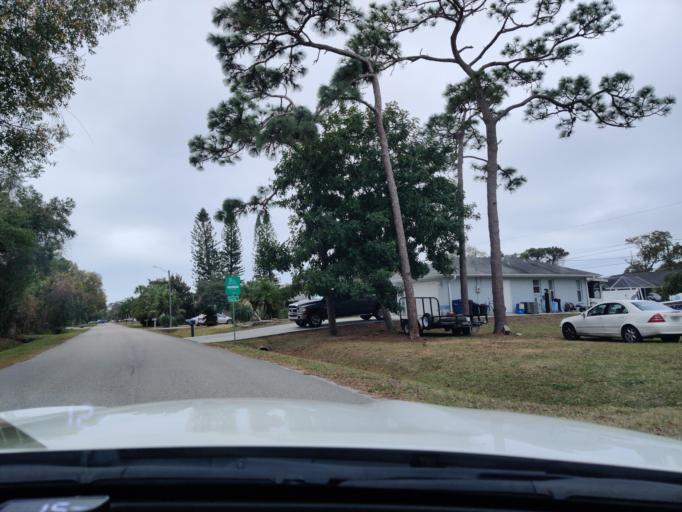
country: US
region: Florida
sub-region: Sarasota County
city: South Venice
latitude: 27.0459
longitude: -82.4048
